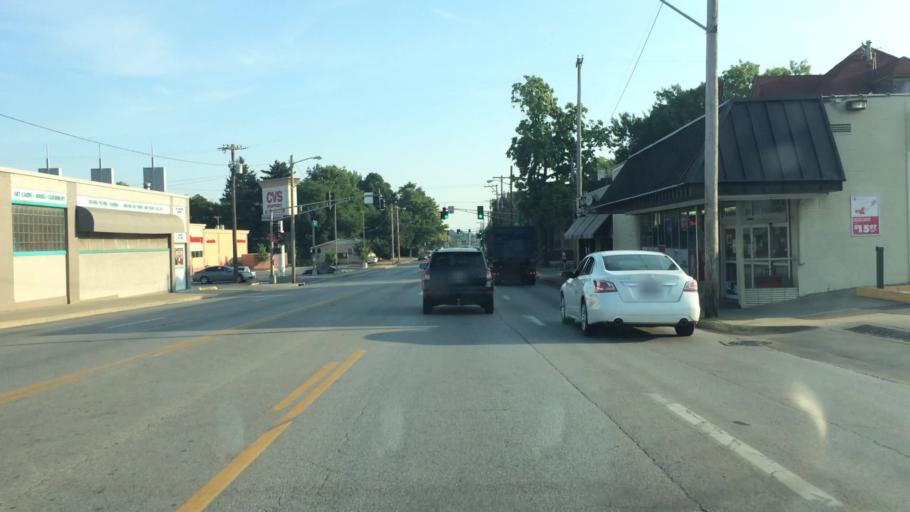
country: US
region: Missouri
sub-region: Greene County
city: Springfield
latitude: 37.2045
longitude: -93.2761
